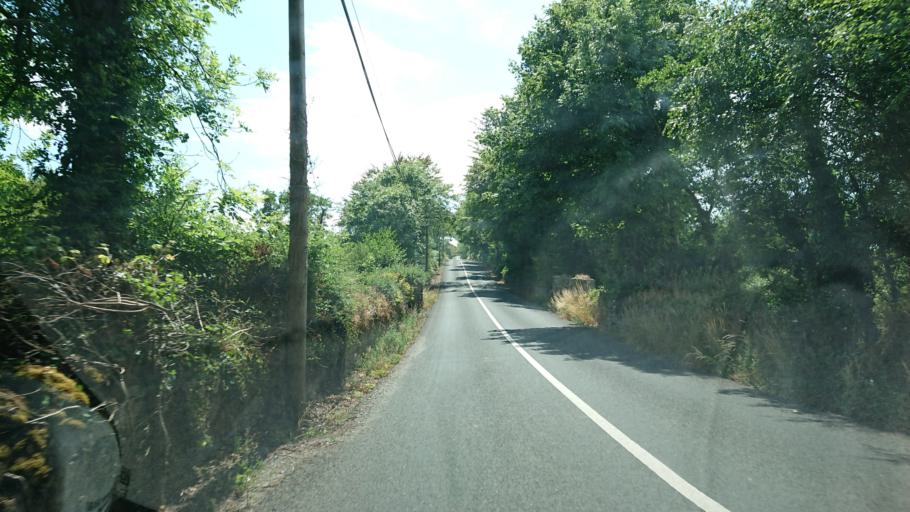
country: IE
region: Munster
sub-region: Waterford
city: Portlaw
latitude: 52.1672
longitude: -7.3374
